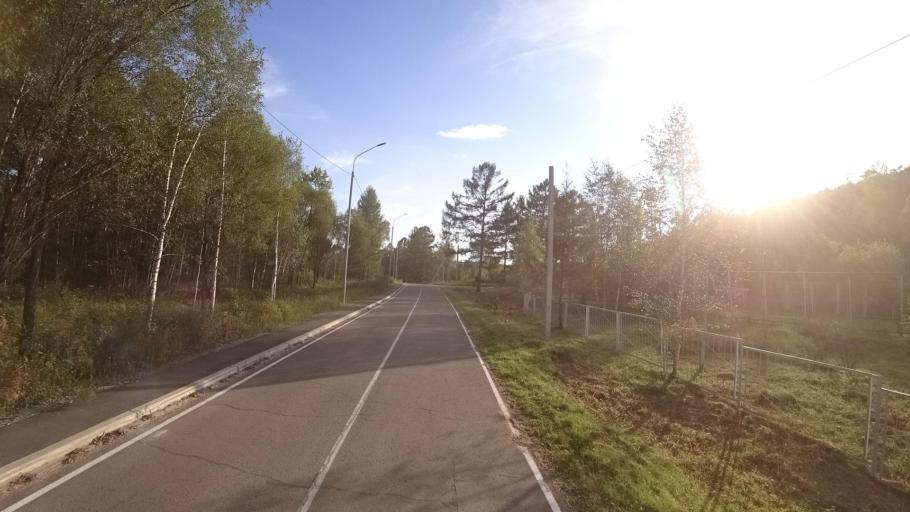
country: RU
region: Jewish Autonomous Oblast
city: Kul'dur
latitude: 49.2061
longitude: 131.6213
